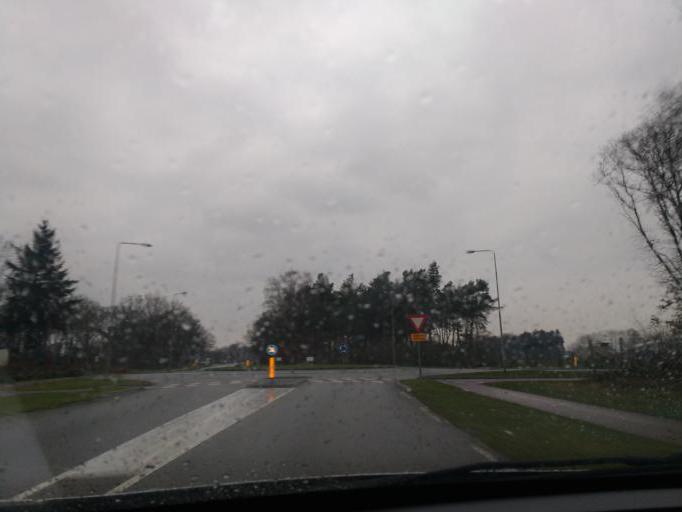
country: NL
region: Limburg
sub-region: Gemeente Venray
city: Venray
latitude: 51.5341
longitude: 5.9564
